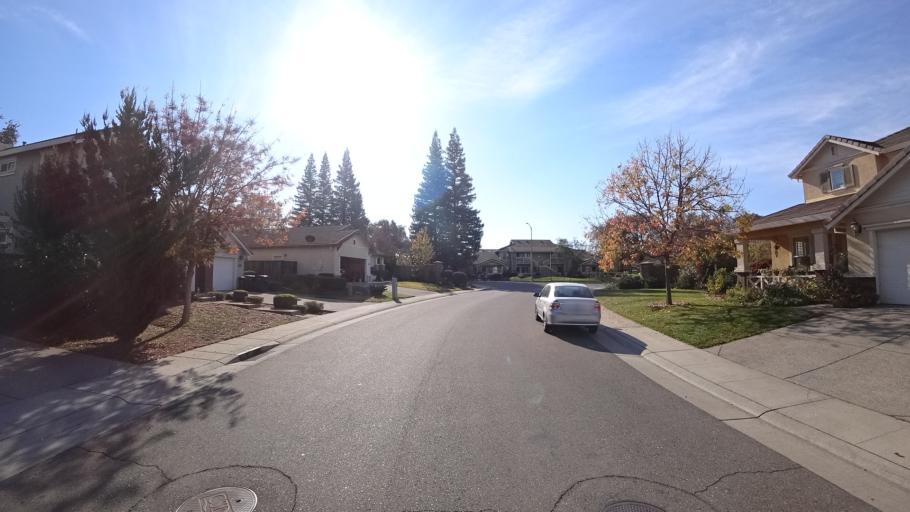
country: US
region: California
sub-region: Sacramento County
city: Citrus Heights
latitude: 38.6825
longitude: -121.2942
